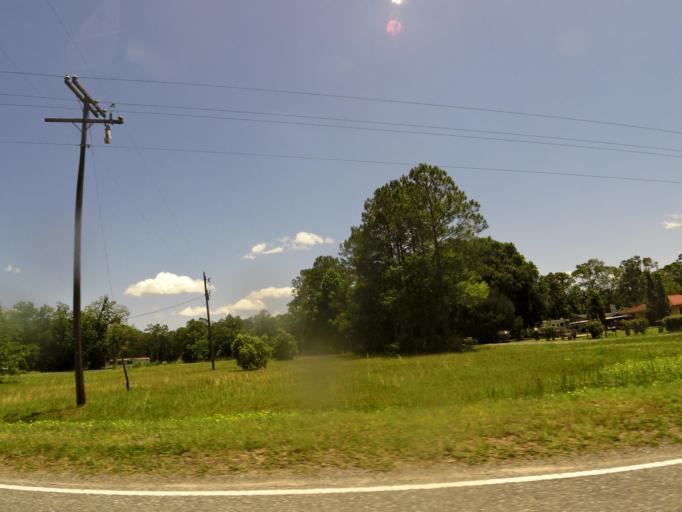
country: US
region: Florida
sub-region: Bradford County
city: Starke
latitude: 30.0257
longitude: -82.0736
